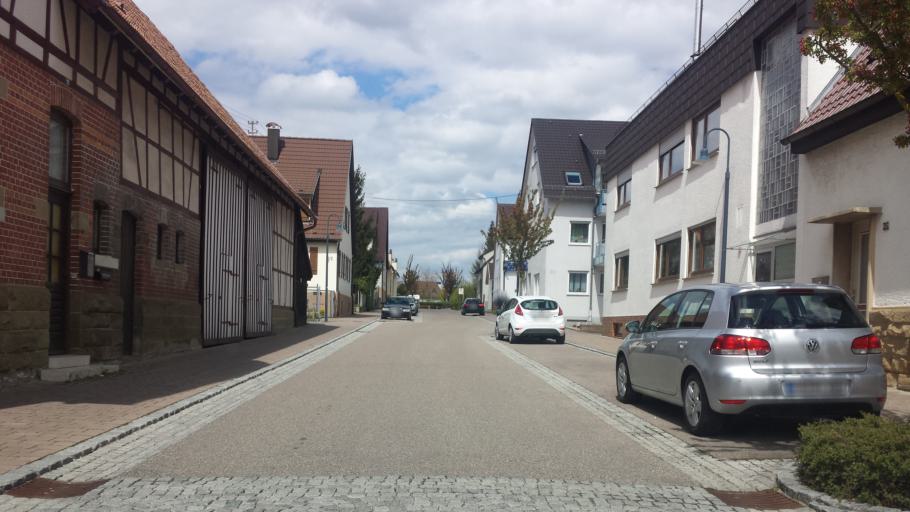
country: DE
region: Baden-Wuerttemberg
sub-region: Regierungsbezirk Stuttgart
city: Rutesheim
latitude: 48.8109
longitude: 8.9427
